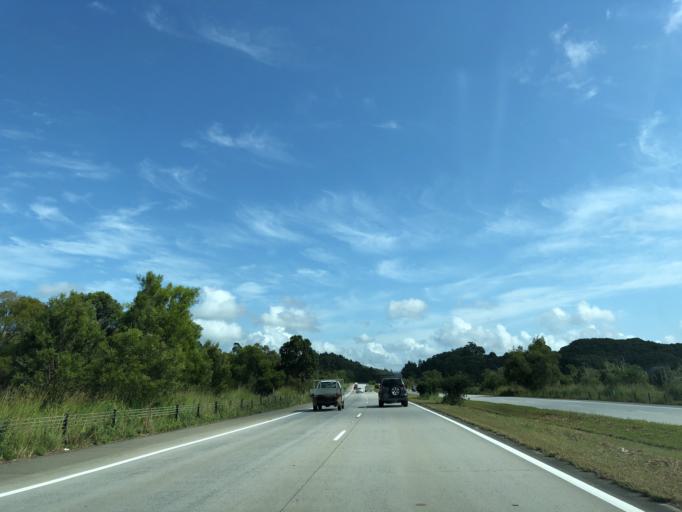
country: AU
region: New South Wales
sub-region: Byron Shire
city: Brunswick Heads
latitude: -28.5779
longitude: 153.5435
